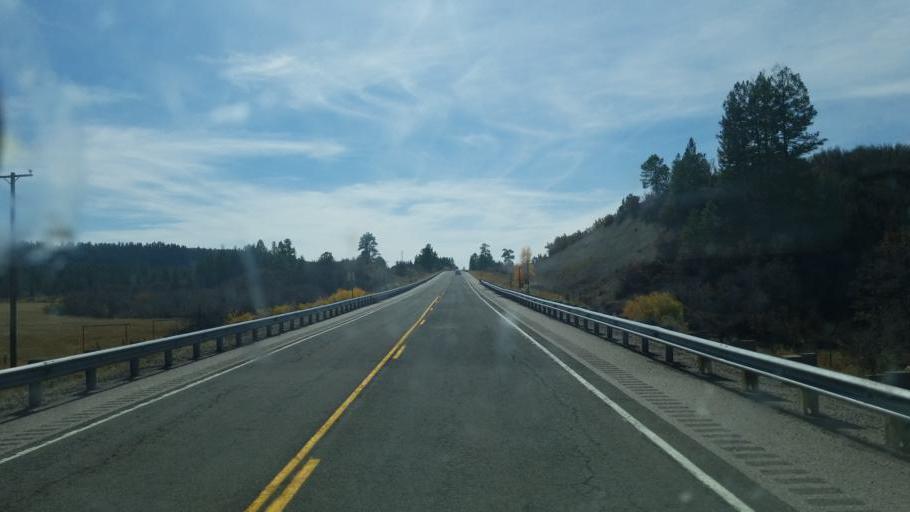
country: US
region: New Mexico
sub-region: Rio Arriba County
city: Chama
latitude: 36.9904
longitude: -106.7810
